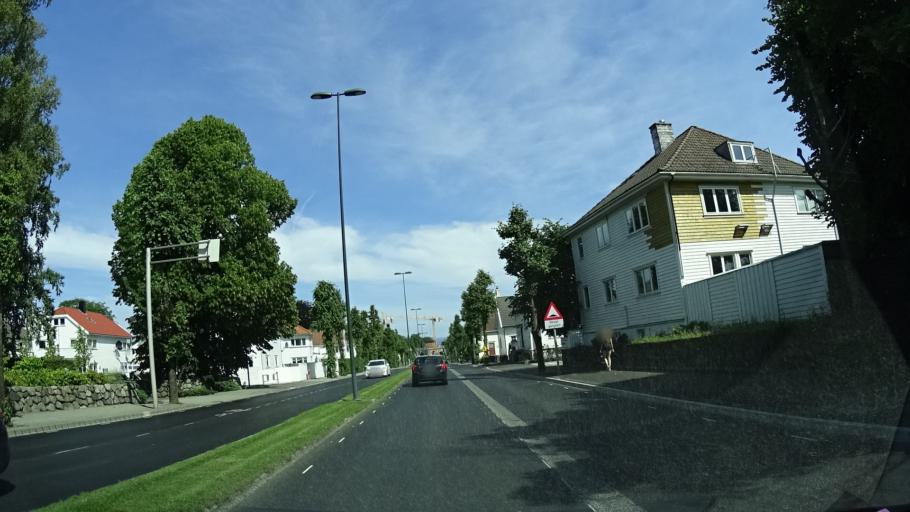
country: NO
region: Rogaland
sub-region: Stavanger
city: Stavanger
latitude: 58.9616
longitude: 5.7173
